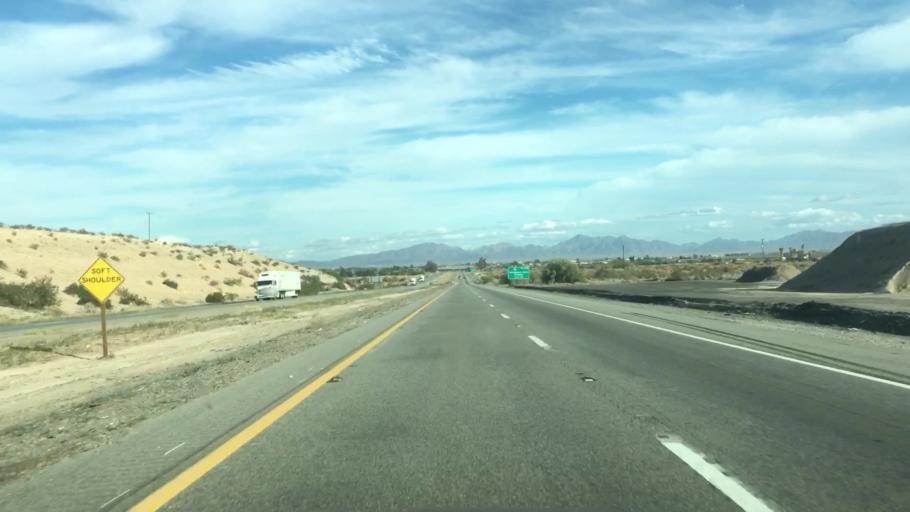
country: US
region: California
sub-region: Riverside County
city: Mesa Verde
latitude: 33.6071
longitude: -114.6736
